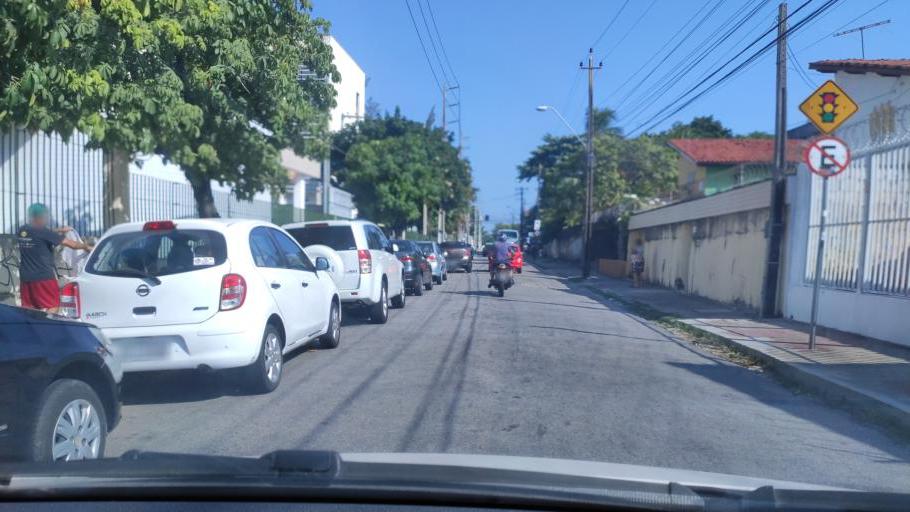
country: BR
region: Ceara
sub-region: Fortaleza
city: Fortaleza
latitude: -3.7406
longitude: -38.5374
